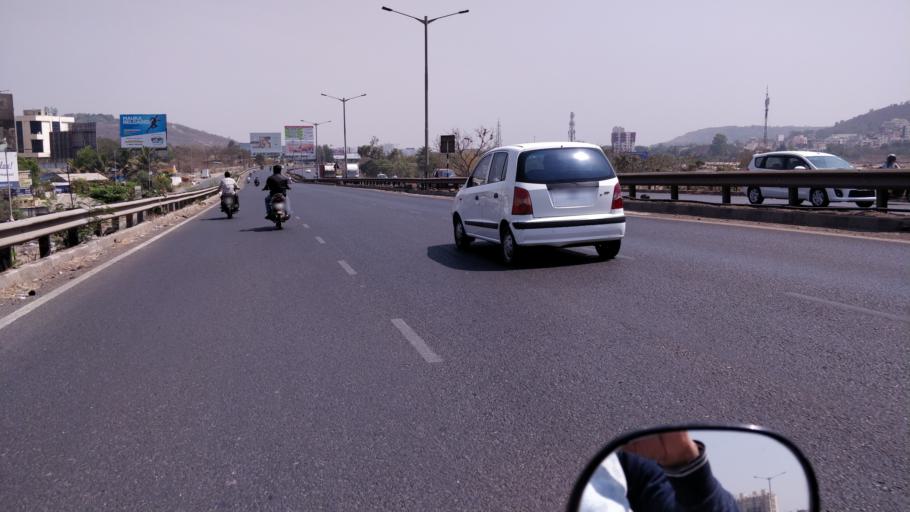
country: IN
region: Maharashtra
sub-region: Pune Division
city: Shivaji Nagar
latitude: 18.5230
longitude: 73.7704
